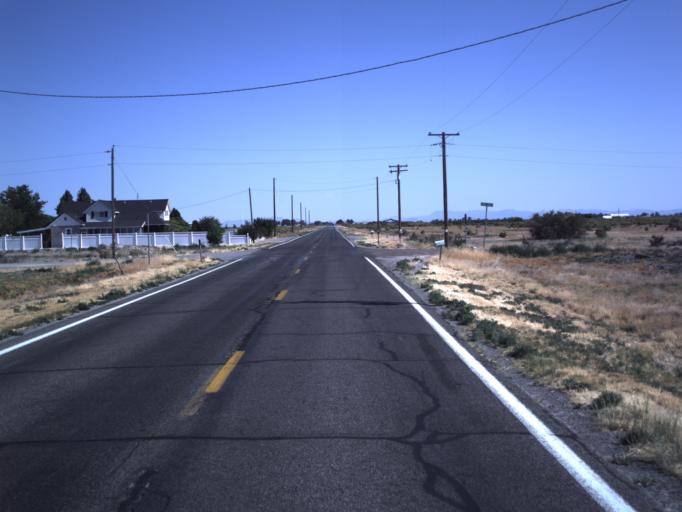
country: US
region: Utah
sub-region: Millard County
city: Delta
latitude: 39.3010
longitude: -112.6525
